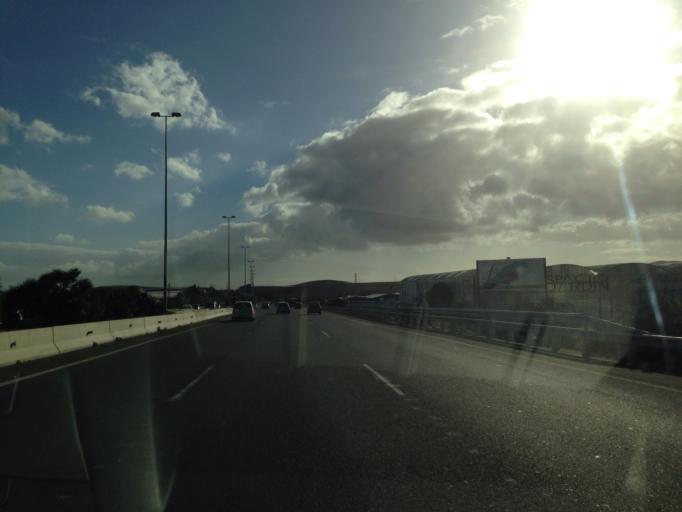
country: ES
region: Canary Islands
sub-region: Provincia de Las Palmas
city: Cruce de Arinaga
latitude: 27.8961
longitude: -15.4059
